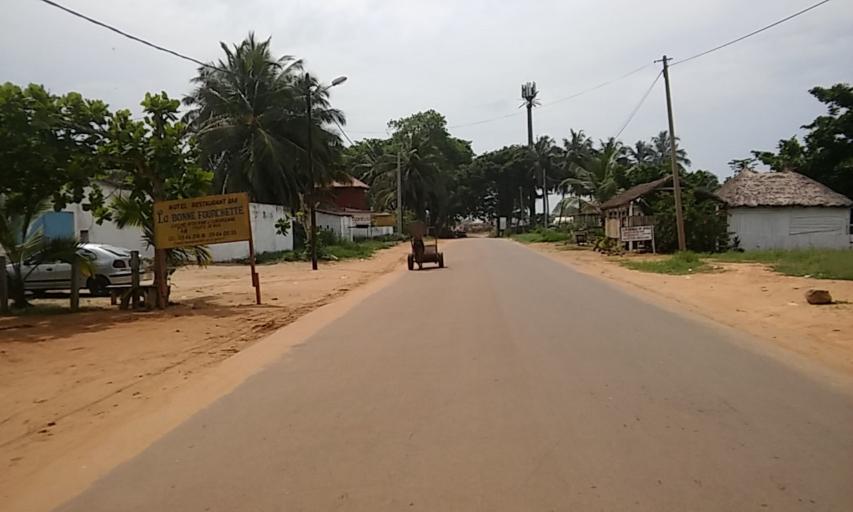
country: CI
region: Sud-Comoe
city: Grand-Bassam
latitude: 5.1968
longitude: -3.7459
